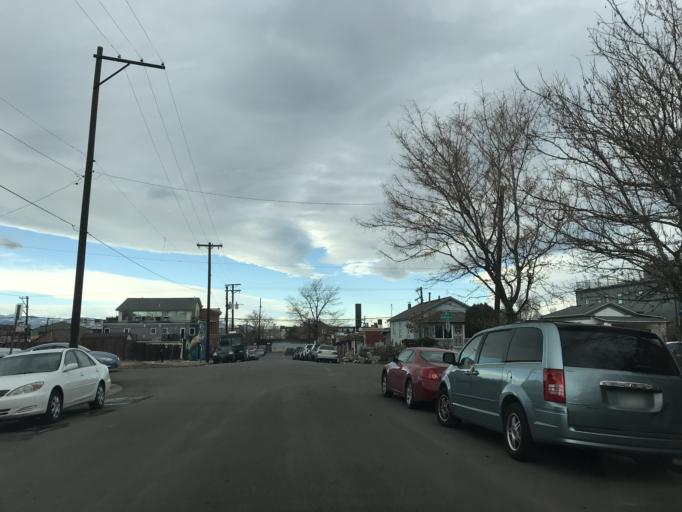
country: US
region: Colorado
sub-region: Denver County
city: Denver
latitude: 39.7624
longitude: -104.9782
